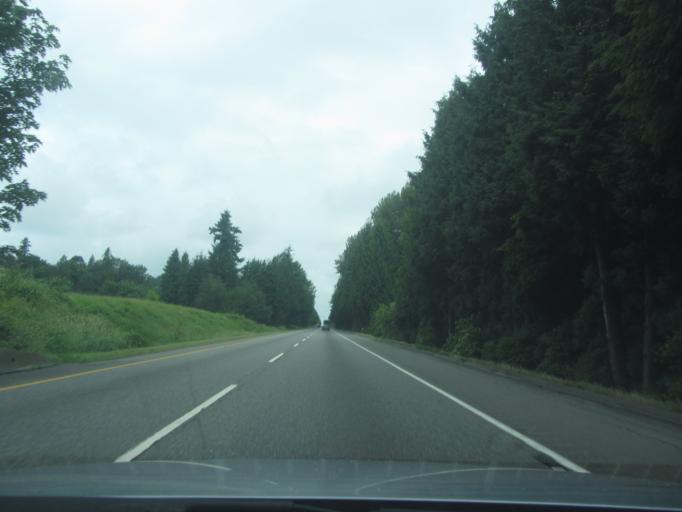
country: CA
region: British Columbia
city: Aldergrove
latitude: 49.0948
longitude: -122.4751
